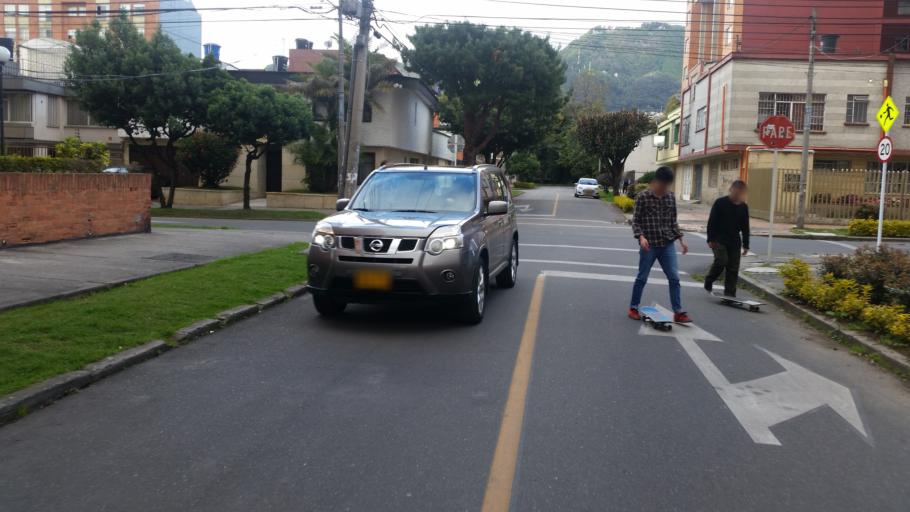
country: CO
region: Bogota D.C.
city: Bogota
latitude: 4.6371
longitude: -74.0781
